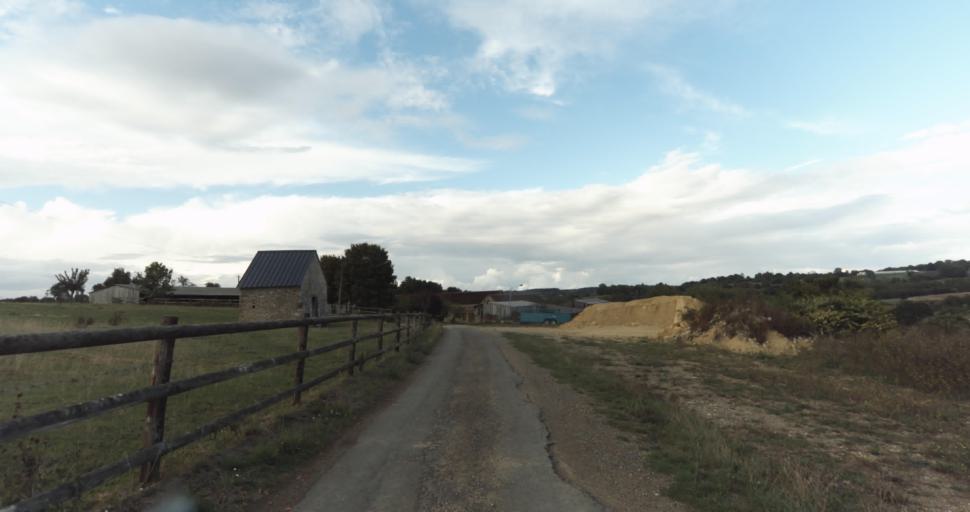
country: FR
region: Lower Normandy
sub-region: Departement de l'Orne
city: Gace
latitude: 48.7560
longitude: 0.3630
